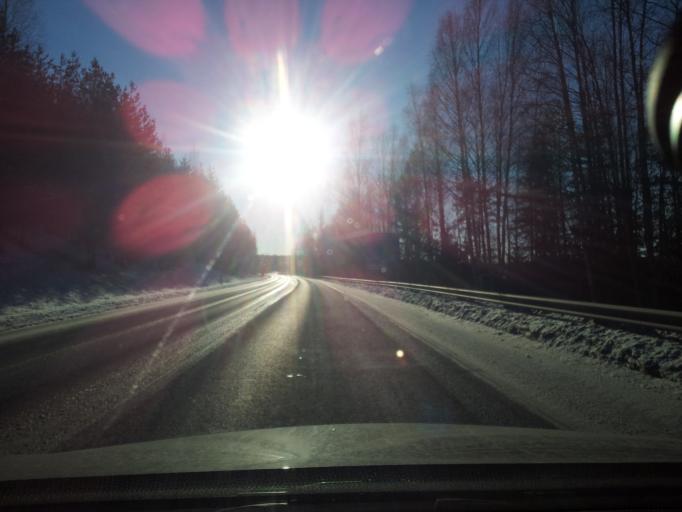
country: FI
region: Uusimaa
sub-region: Helsinki
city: Vihti
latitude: 60.3566
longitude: 24.3382
